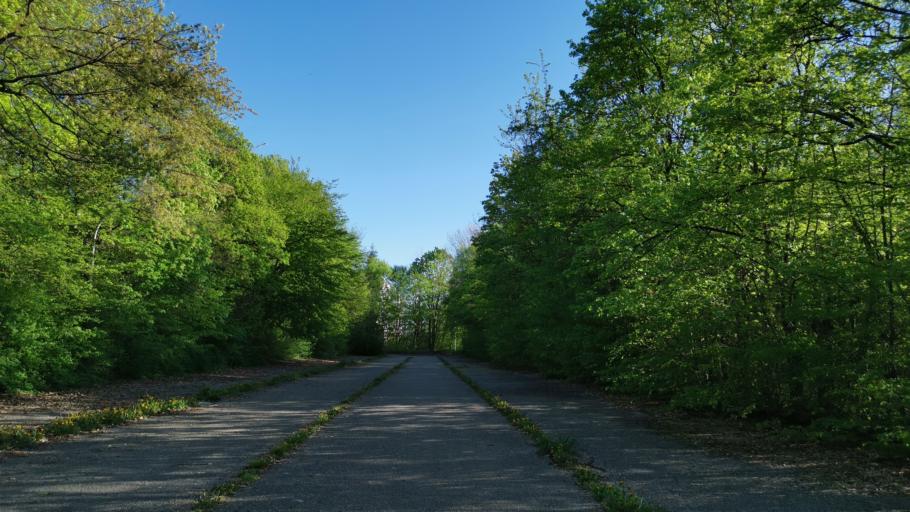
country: DE
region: Bavaria
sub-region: Upper Bavaria
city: Pullach im Isartal
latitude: 48.0896
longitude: 11.5305
